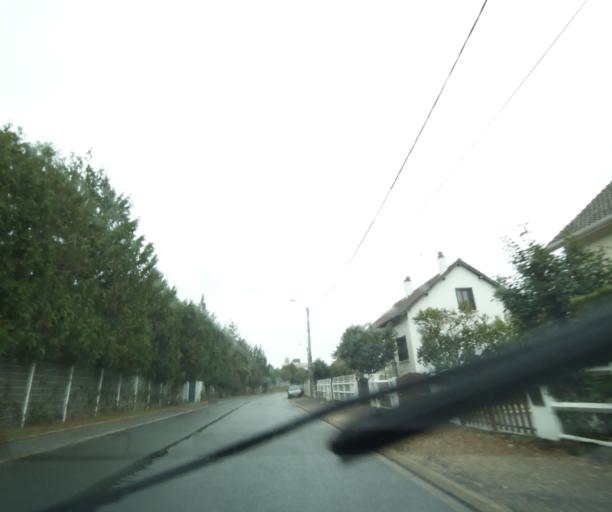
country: FR
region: Centre
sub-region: Departement d'Eure-et-Loir
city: Vernouillet
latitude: 48.7275
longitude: 1.3823
